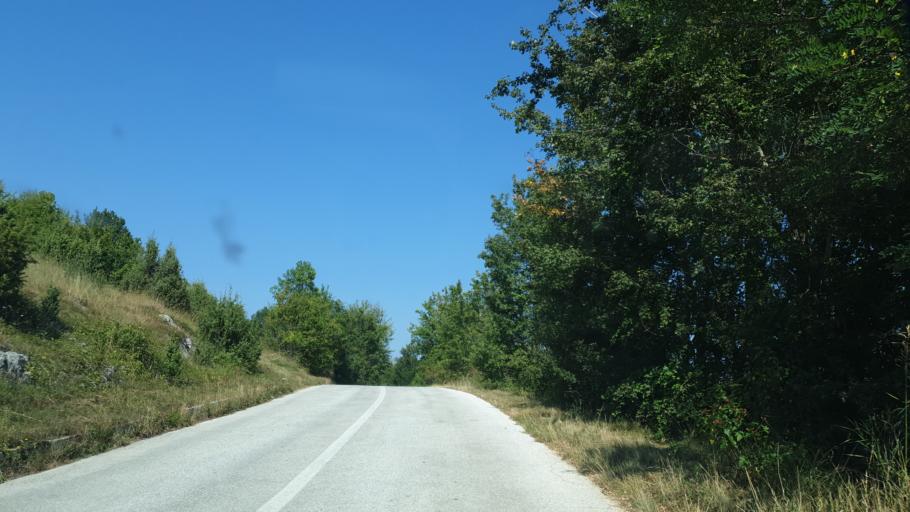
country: RS
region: Central Serbia
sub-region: Zlatiborski Okrug
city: Cajetina
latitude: 43.6818
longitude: 19.8468
